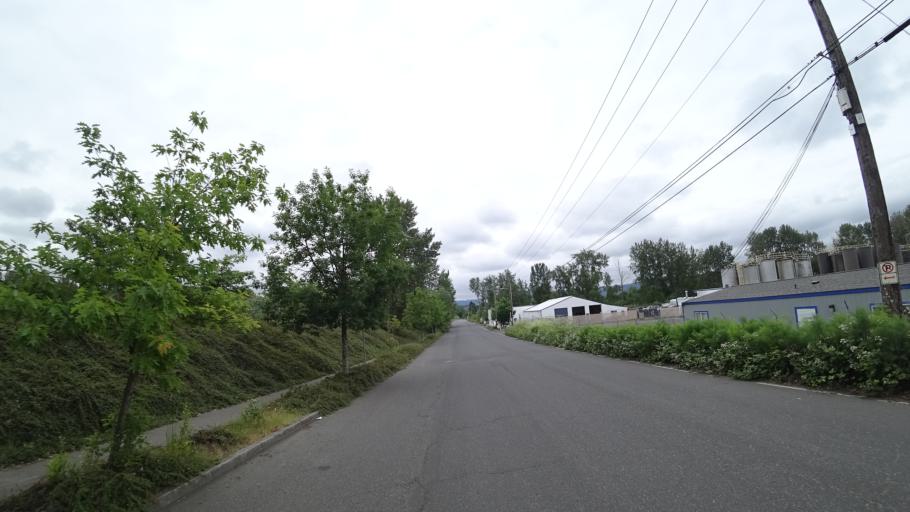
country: US
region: Washington
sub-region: Clark County
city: Vancouver
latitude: 45.6070
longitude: -122.6923
